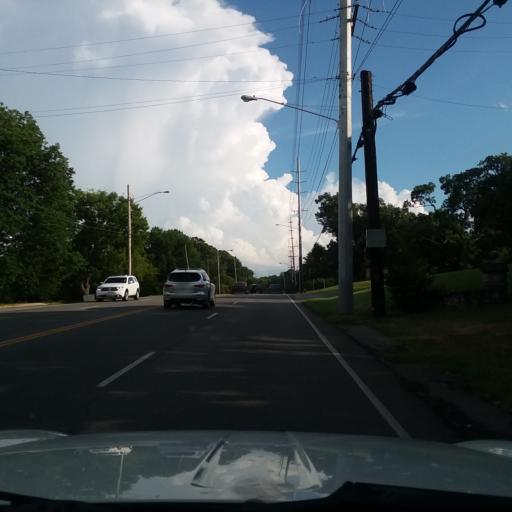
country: US
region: Tennessee
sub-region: Davidson County
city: Oak Hill
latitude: 36.0770
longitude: -86.7733
